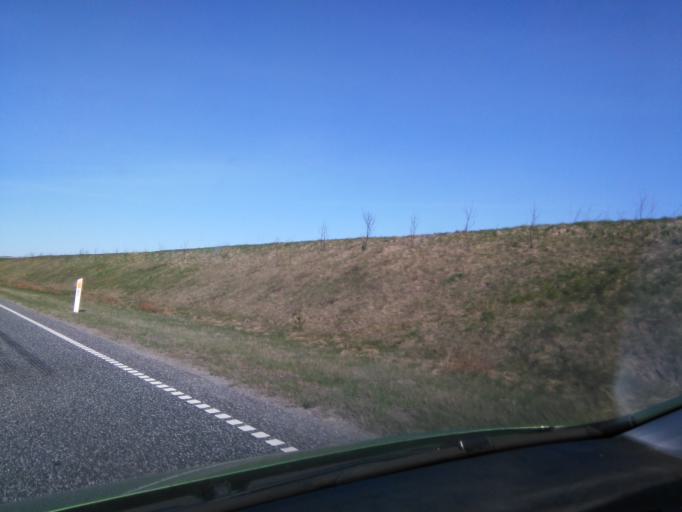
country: DK
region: Central Jutland
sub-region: Hedensted Kommune
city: Torring
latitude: 55.8417
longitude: 9.5818
